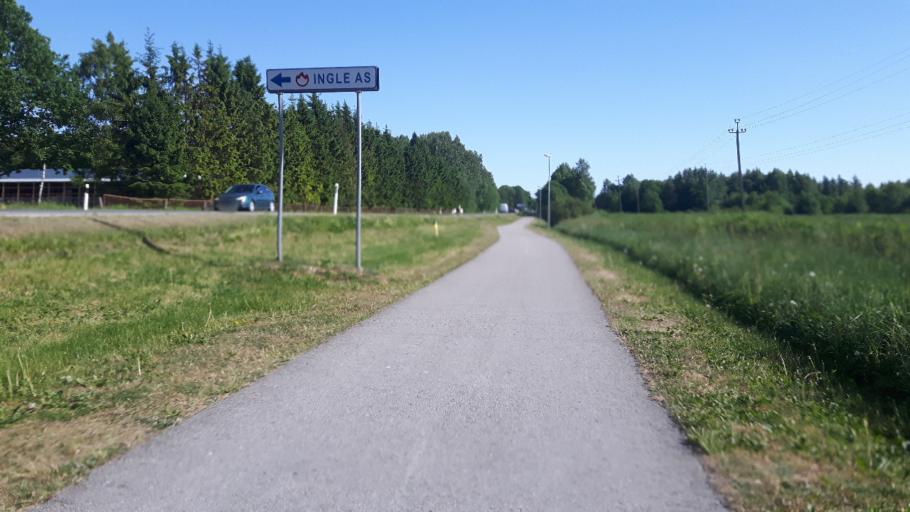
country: EE
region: Raplamaa
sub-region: Rapla vald
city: Rapla
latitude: 58.9842
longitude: 24.8424
